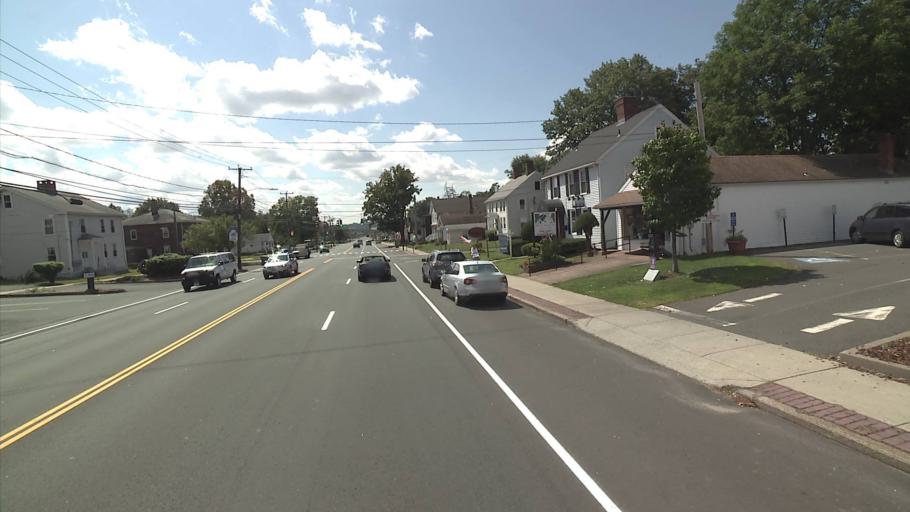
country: US
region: Connecticut
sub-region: Middlesex County
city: Portland
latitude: 41.5752
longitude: -72.6391
